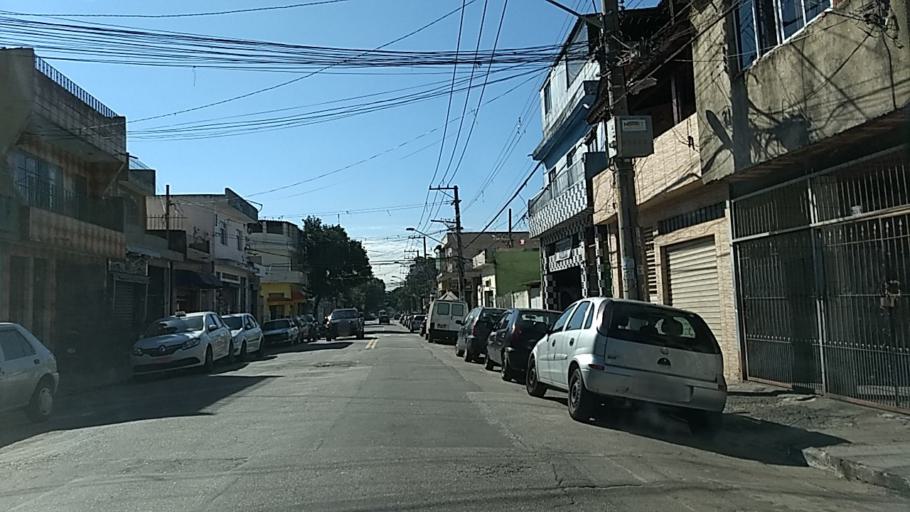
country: BR
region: Sao Paulo
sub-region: Guarulhos
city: Guarulhos
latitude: -23.4819
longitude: -46.5729
